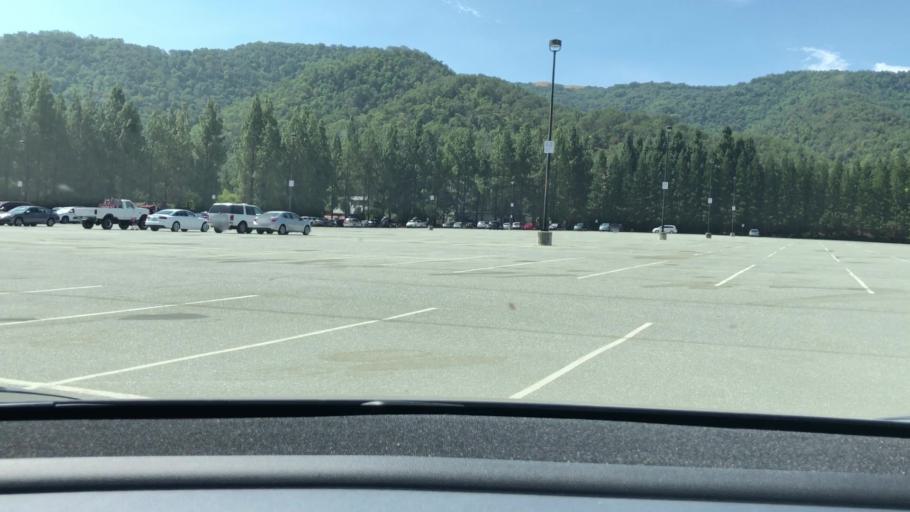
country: US
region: California
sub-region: Santa Clara County
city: Gilroy
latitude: 37.0074
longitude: -121.6310
